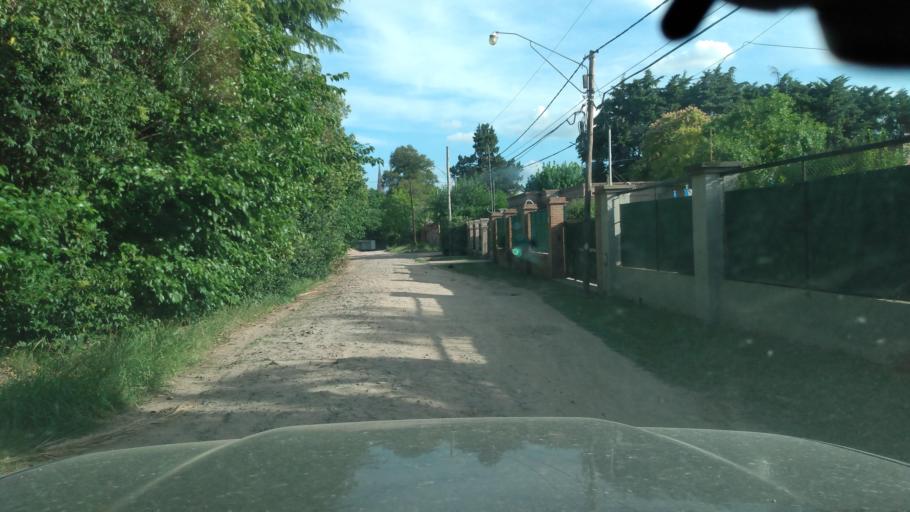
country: AR
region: Buenos Aires
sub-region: Partido de Lujan
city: Lujan
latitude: -34.5572
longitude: -59.1265
